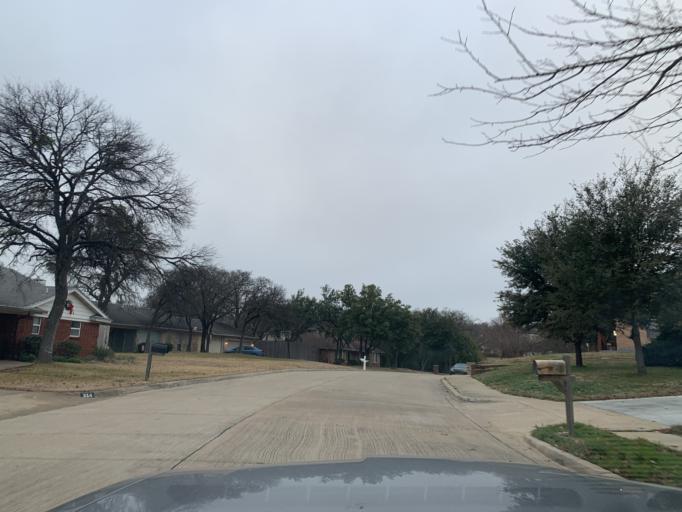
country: US
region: Texas
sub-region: Tarrant County
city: Bedford
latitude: 32.8386
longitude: -97.1533
